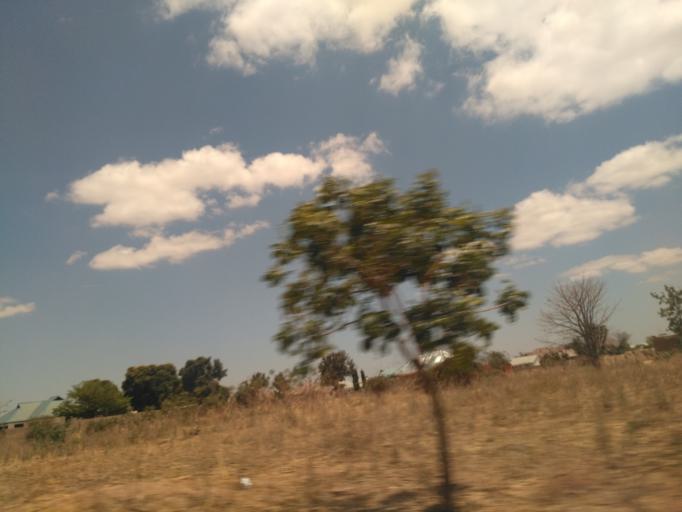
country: TZ
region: Dodoma
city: Kisasa
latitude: -6.1718
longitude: 35.7900
